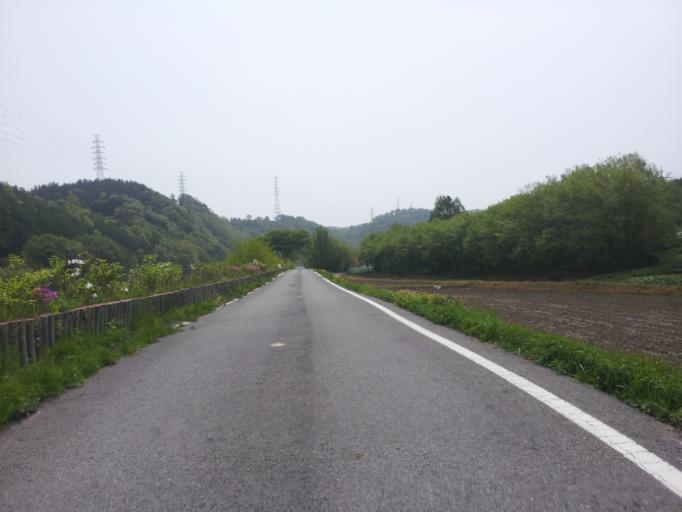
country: KR
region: Daejeon
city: Daejeon
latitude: 36.2622
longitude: 127.2955
